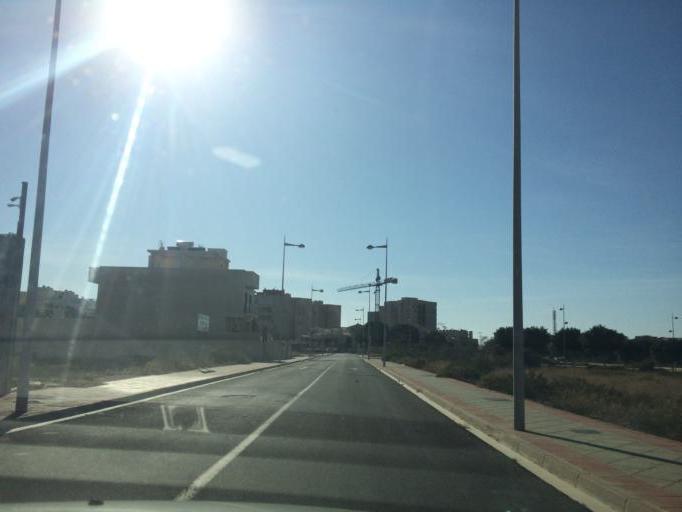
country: ES
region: Andalusia
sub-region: Provincia de Almeria
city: Almeria
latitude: 36.8265
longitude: -2.4396
